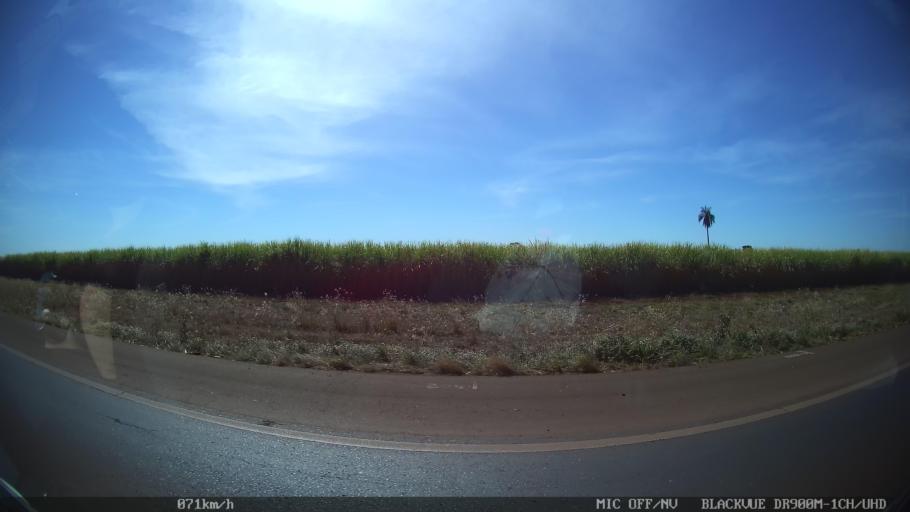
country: BR
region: Sao Paulo
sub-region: Ipua
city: Ipua
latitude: -20.5051
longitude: -47.9322
